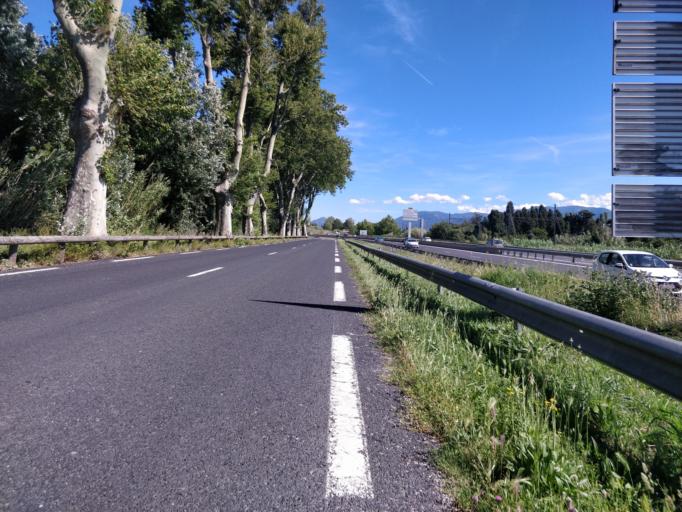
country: FR
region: Languedoc-Roussillon
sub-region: Departement des Pyrenees-Orientales
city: Corneilla-del-Vercol
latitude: 42.6194
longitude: 2.9536
